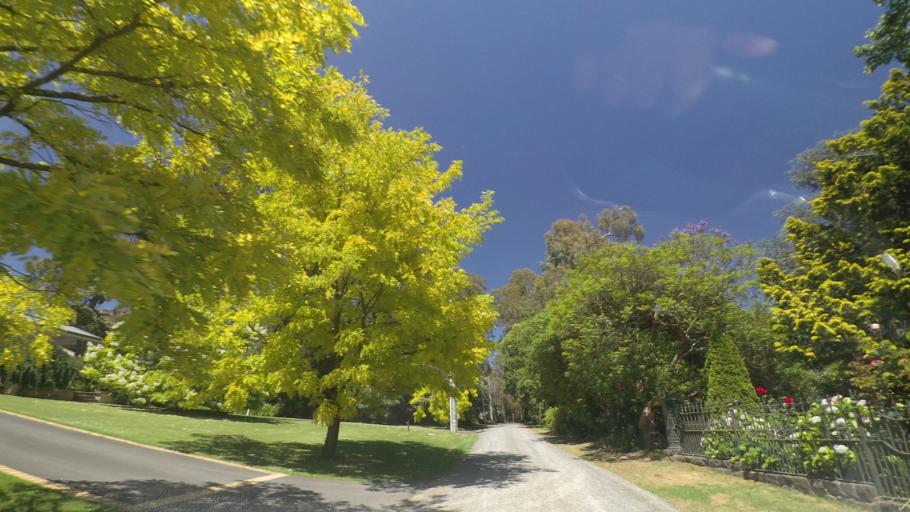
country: AU
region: Victoria
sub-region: Yarra Ranges
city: Montrose
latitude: -37.8114
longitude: 145.3476
